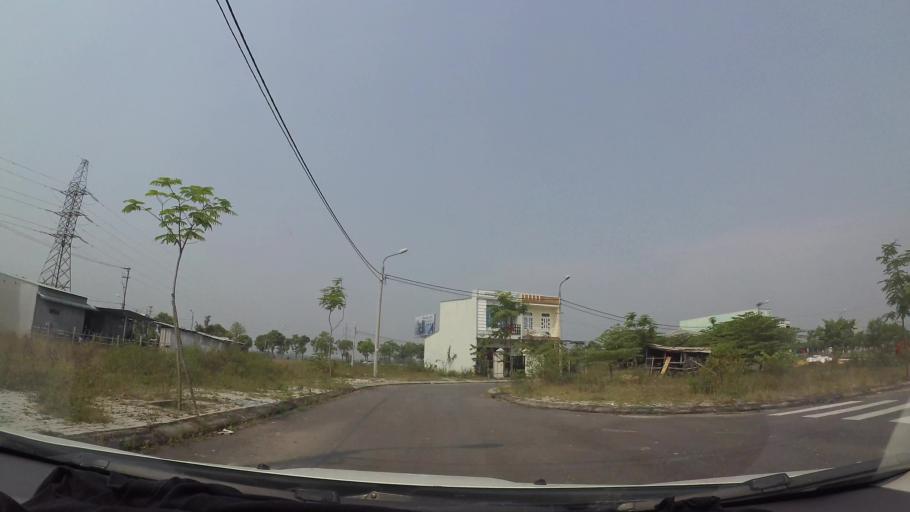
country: VN
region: Da Nang
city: Cam Le
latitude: 15.9705
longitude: 108.2106
